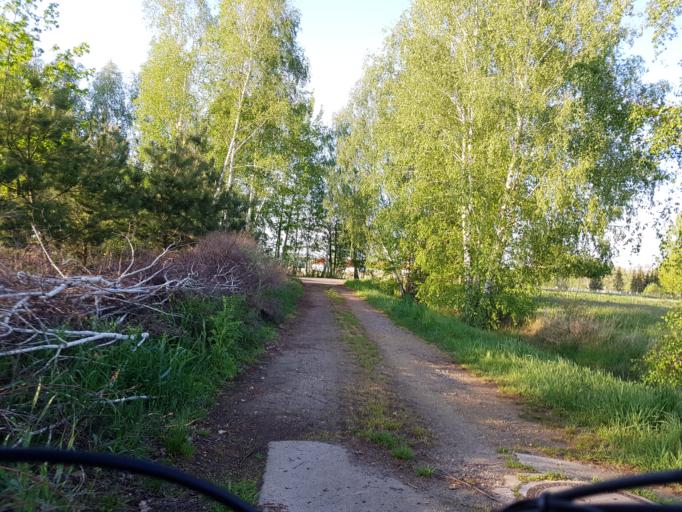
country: DE
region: Brandenburg
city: Schilda
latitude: 51.5753
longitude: 13.4023
